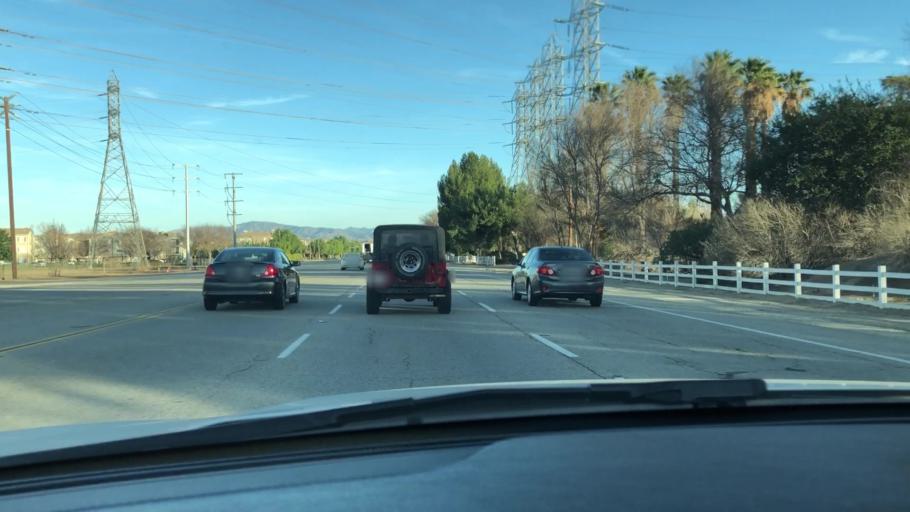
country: US
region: California
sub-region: Los Angeles County
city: Valencia
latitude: 34.4236
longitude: -118.5751
